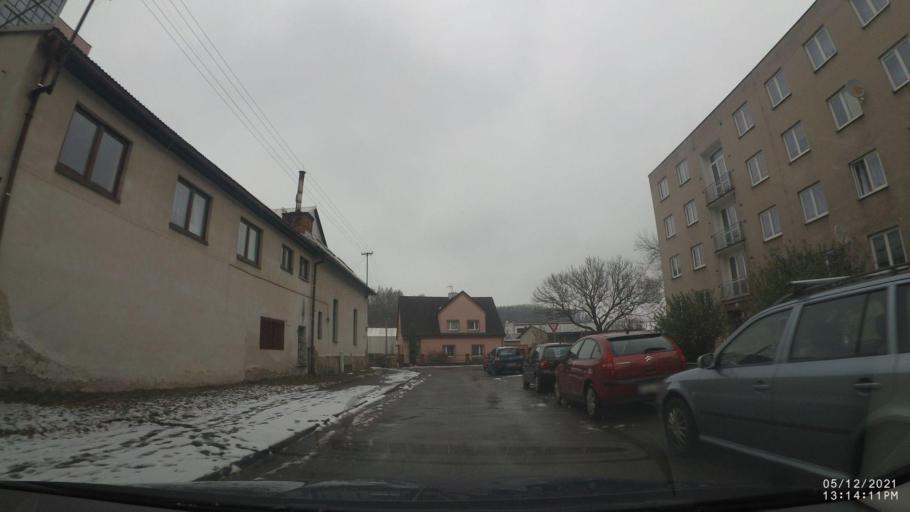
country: CZ
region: Kralovehradecky
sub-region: Okres Nachod
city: Nachod
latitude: 50.4173
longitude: 16.1800
